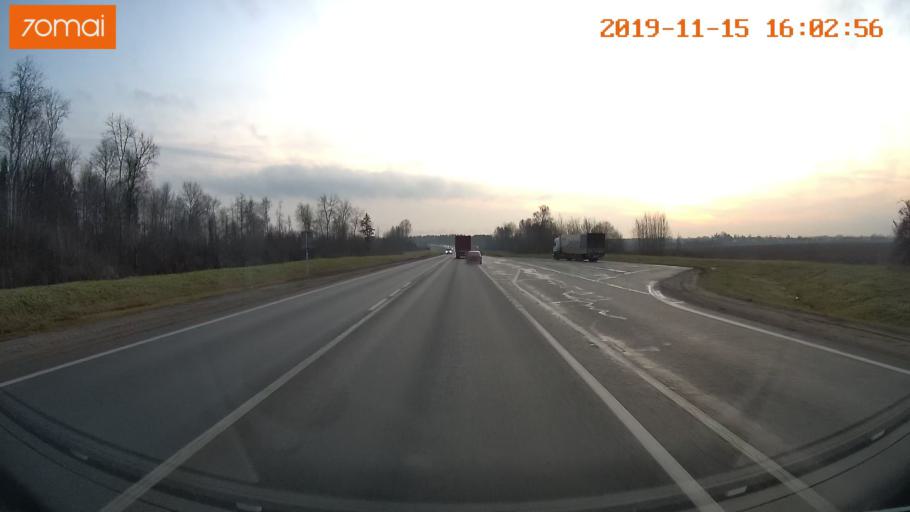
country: RU
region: Jaroslavl
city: Yaroslavl
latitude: 57.7661
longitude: 39.9193
